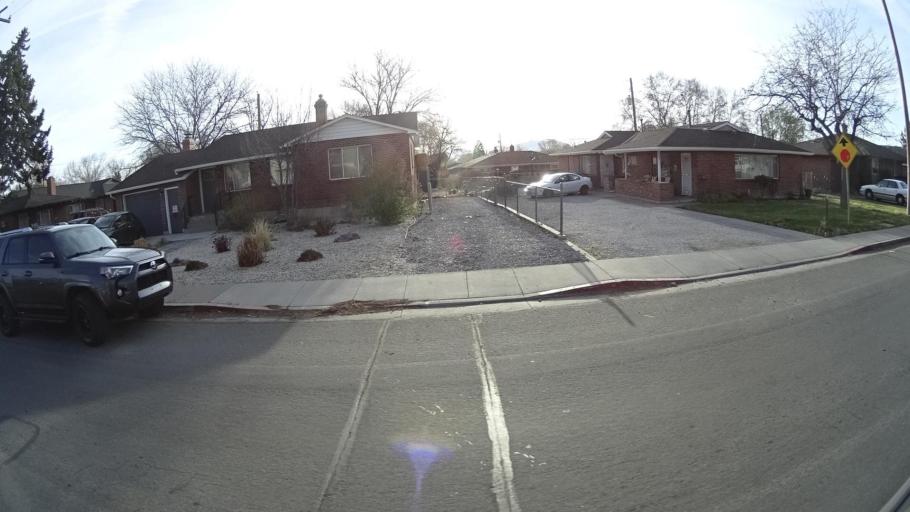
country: US
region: Nevada
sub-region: Washoe County
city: Reno
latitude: 39.5181
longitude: -119.7985
